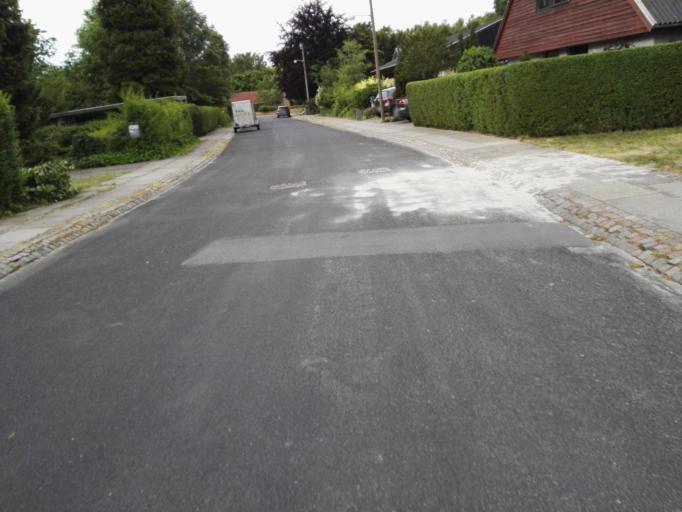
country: DK
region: Capital Region
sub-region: Ballerup Kommune
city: Ballerup
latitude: 55.7476
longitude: 12.3669
